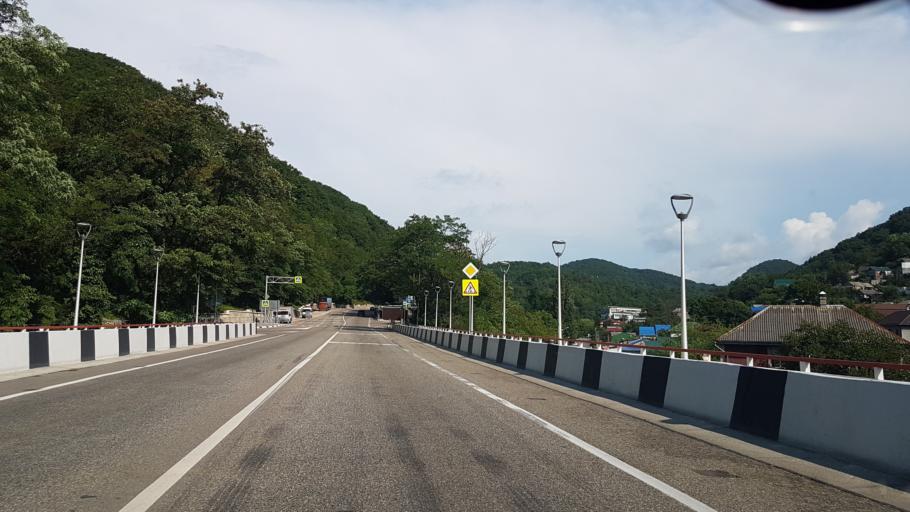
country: RU
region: Krasnodarskiy
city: Tuapse
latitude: 44.1135
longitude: 39.0589
